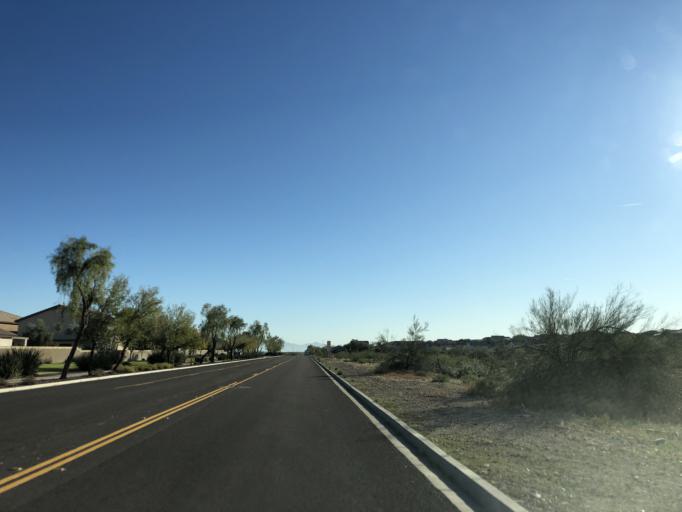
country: US
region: Arizona
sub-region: Maricopa County
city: Sun City West
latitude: 33.6888
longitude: -112.3167
